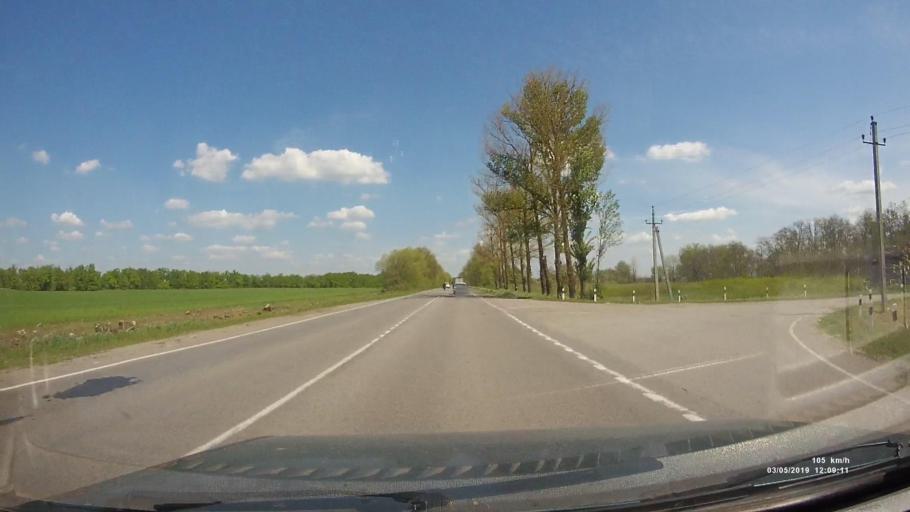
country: RU
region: Rostov
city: Bagayevskaya
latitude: 47.2930
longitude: 40.5114
